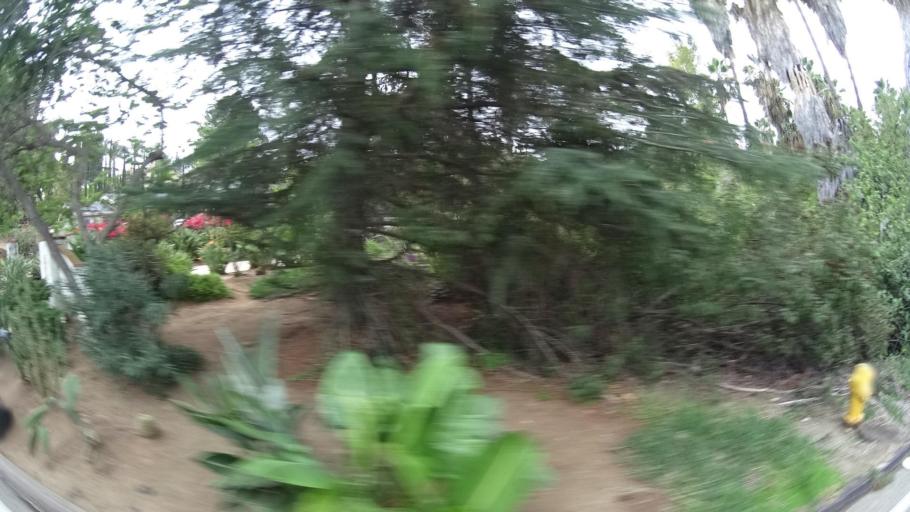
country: US
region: California
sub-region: San Diego County
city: Casa de Oro-Mount Helix
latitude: 32.7616
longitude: -116.9796
